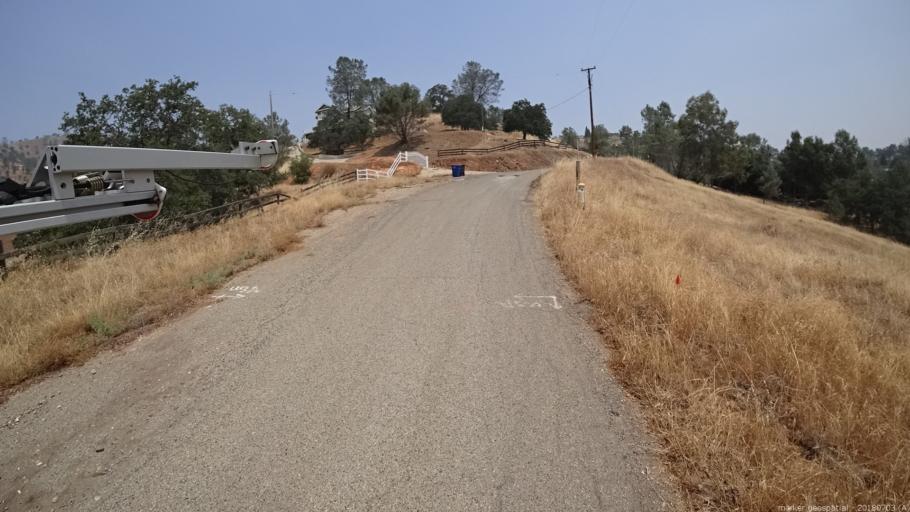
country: US
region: California
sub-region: Fresno County
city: Auberry
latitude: 37.0476
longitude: -119.6536
